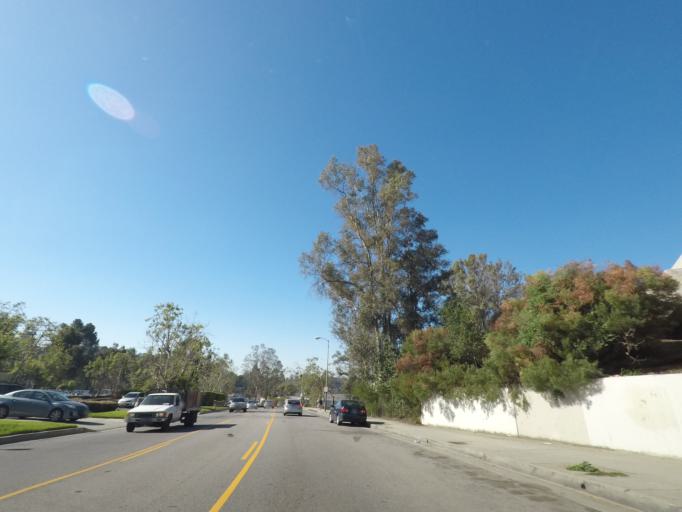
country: US
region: California
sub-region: Los Angeles County
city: Pasadena
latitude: 34.1403
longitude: -118.1870
